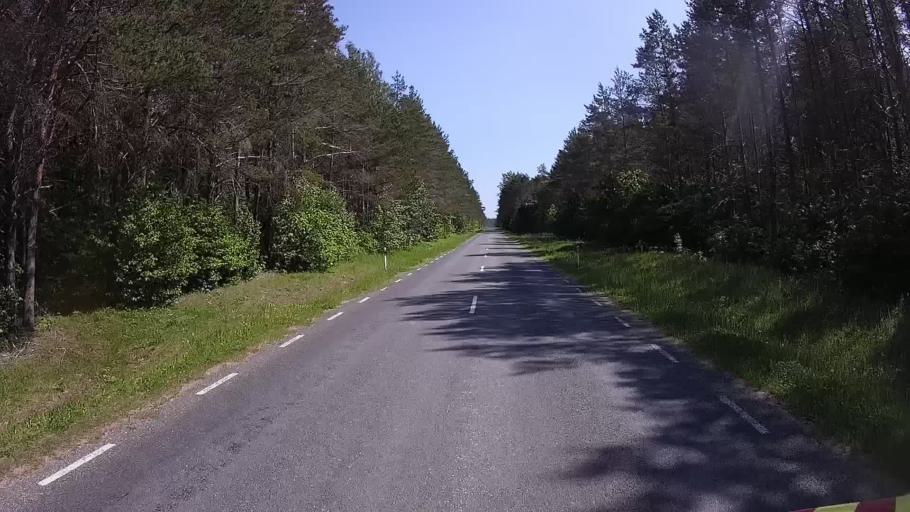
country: EE
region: Saare
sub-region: Kuressaare linn
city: Kuressaare
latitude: 58.5099
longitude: 22.4075
